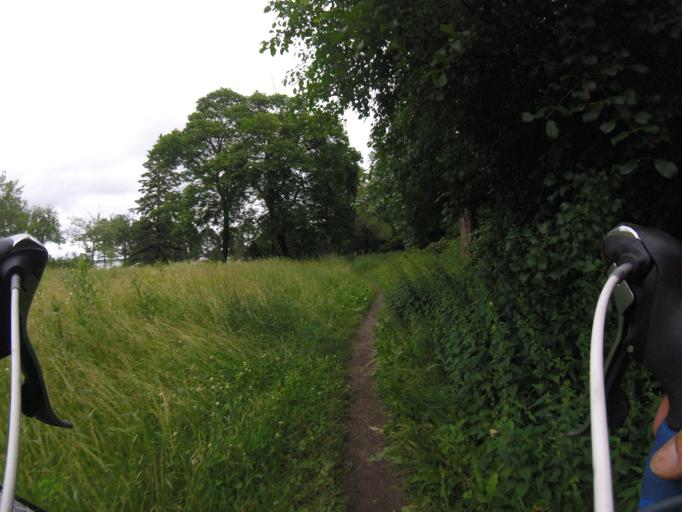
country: CA
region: Ontario
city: Ottawa
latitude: 45.3824
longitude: -75.7747
